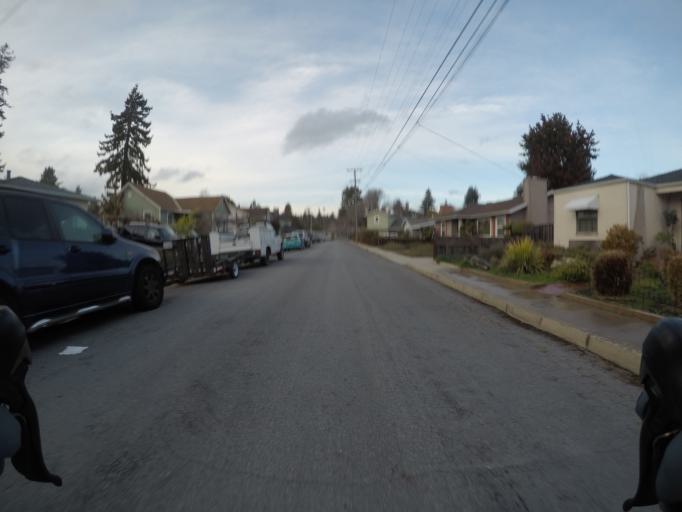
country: US
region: California
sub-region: Santa Cruz County
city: Santa Cruz
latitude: 36.9844
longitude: -122.0182
